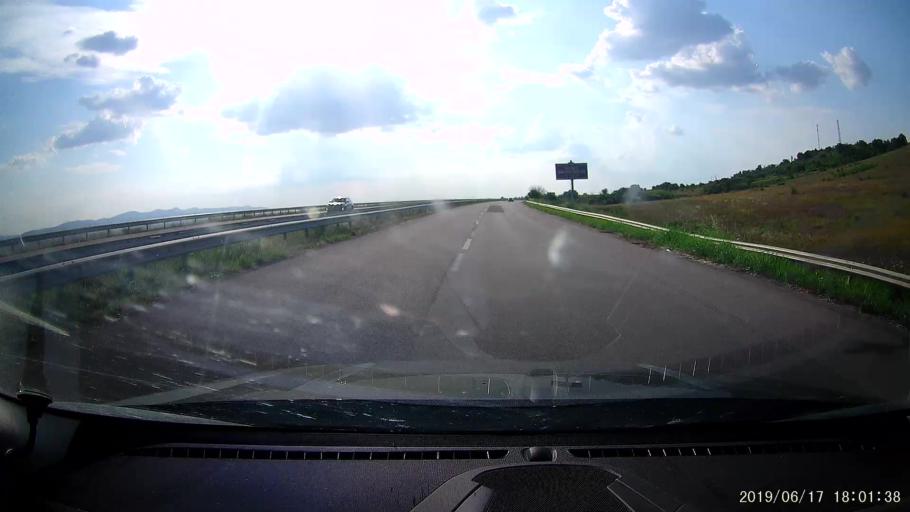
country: BG
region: Khaskovo
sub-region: Obshtina Svilengrad
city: Svilengrad
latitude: 41.7469
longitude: 26.2485
